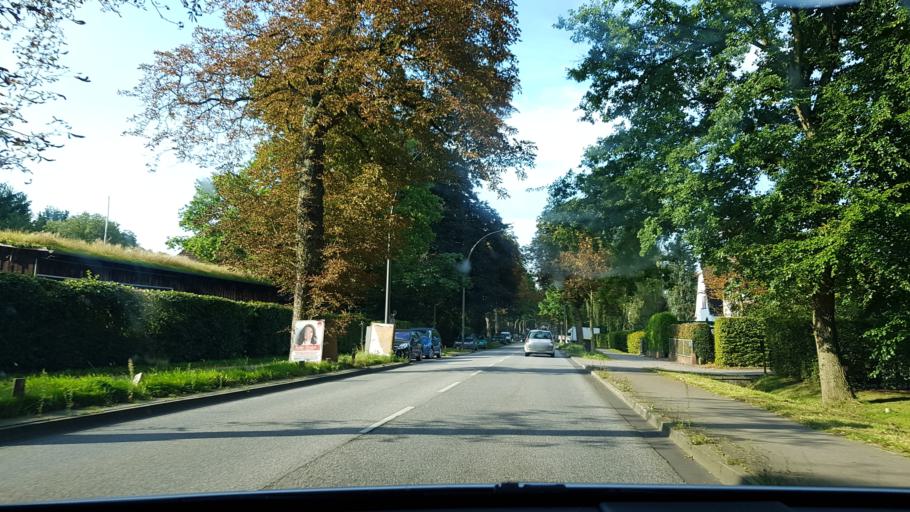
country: DE
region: Hamburg
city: Bergstedt
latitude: 53.6417
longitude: 10.1580
